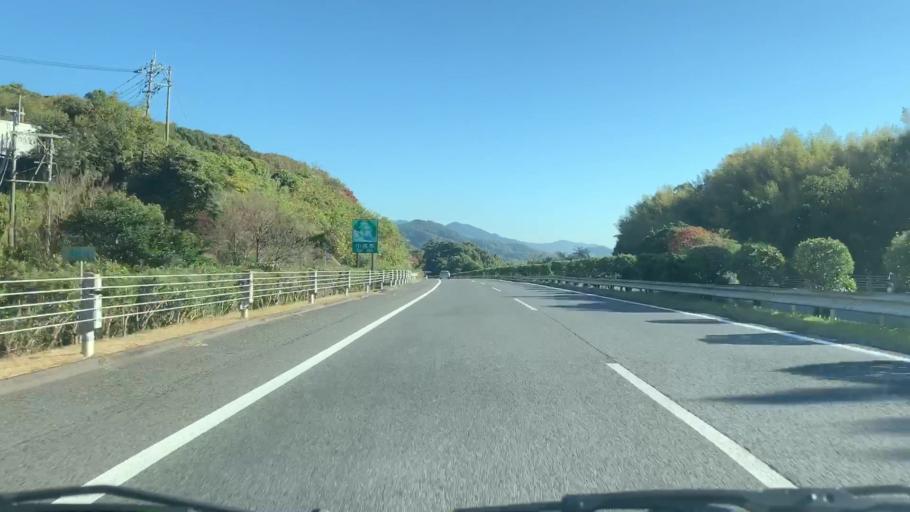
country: JP
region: Saga Prefecture
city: Saga-shi
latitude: 33.2886
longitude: 130.1620
